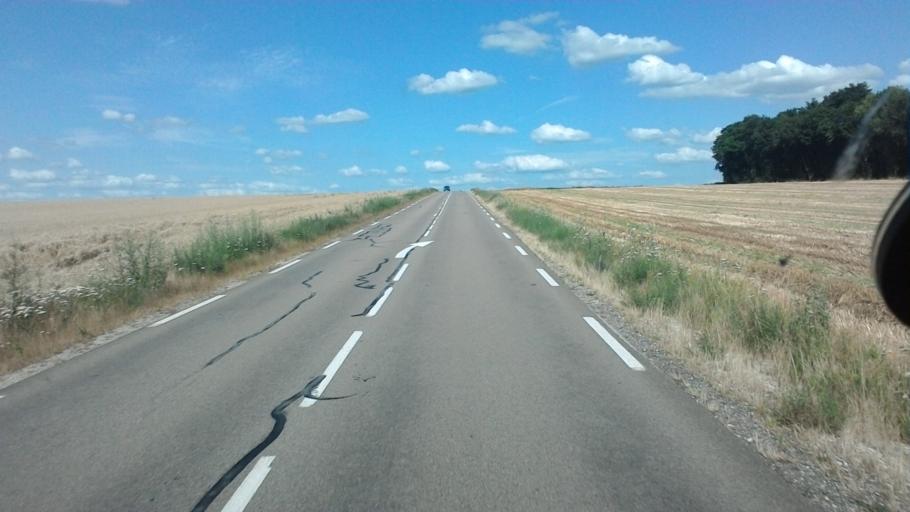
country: FR
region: Franche-Comte
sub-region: Departement de la Haute-Saone
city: Marnay
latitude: 47.3634
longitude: 5.7402
